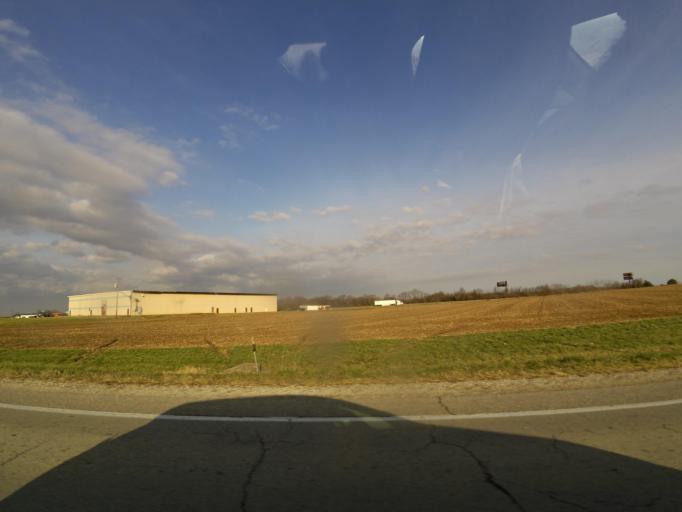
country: US
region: Illinois
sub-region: Fayette County
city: Vandalia
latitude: 38.9743
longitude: -89.1208
